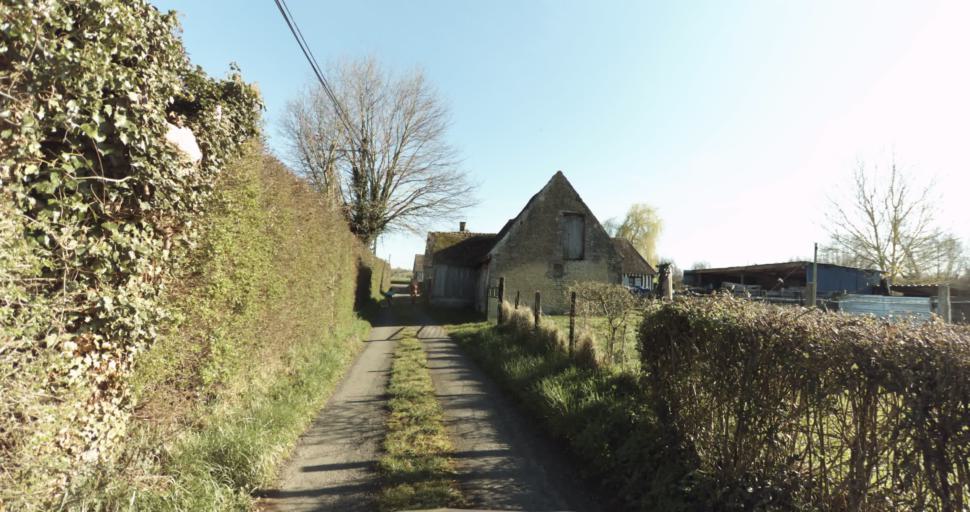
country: FR
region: Lower Normandy
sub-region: Departement du Calvados
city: Saint-Pierre-sur-Dives
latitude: 49.0432
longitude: 0.0595
